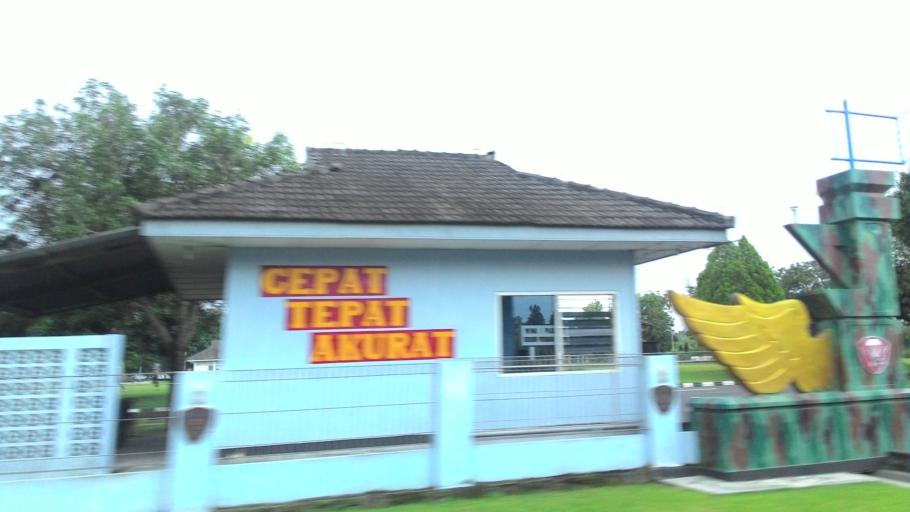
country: ID
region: Daerah Istimewa Yogyakarta
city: Depok
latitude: -7.8042
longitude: 110.4239
